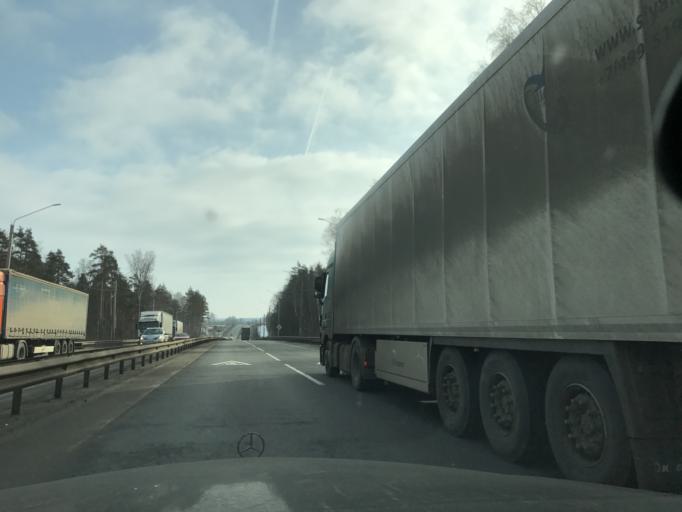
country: RU
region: Vladimir
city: Vyazniki
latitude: 56.2202
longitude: 42.1666
